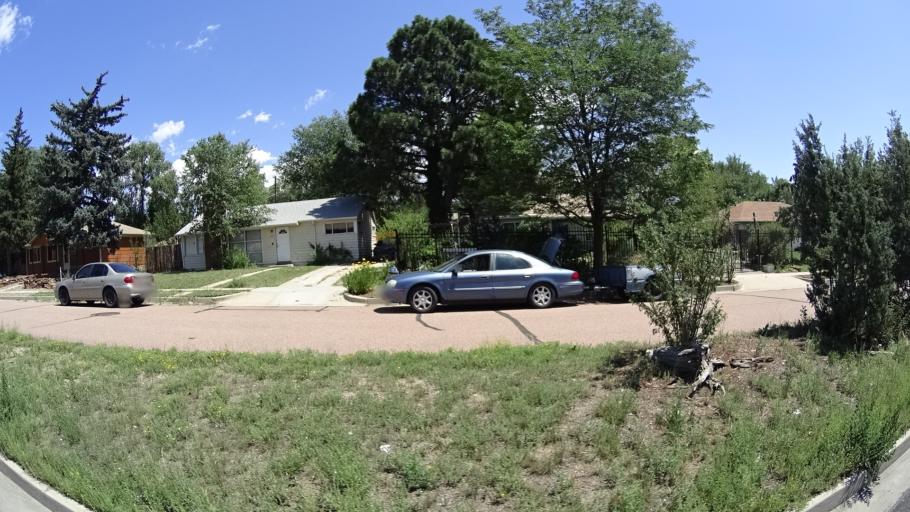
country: US
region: Colorado
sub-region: El Paso County
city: Colorado Springs
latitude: 38.8640
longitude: -104.7941
